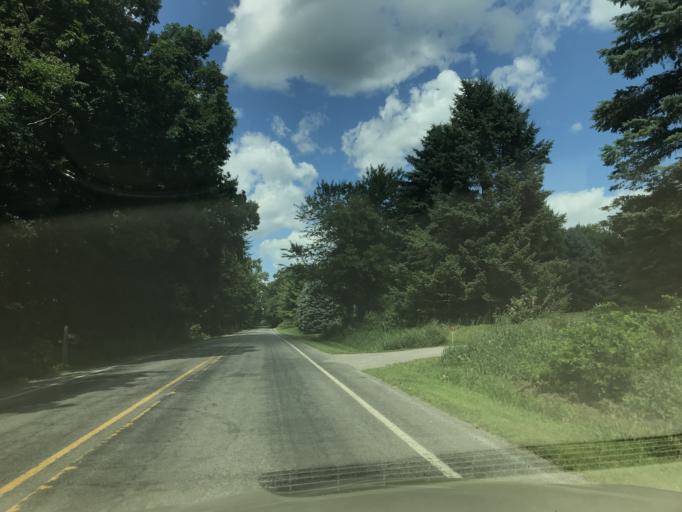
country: US
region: Michigan
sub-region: Eaton County
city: Eaton Rapids
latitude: 42.4526
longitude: -84.5606
